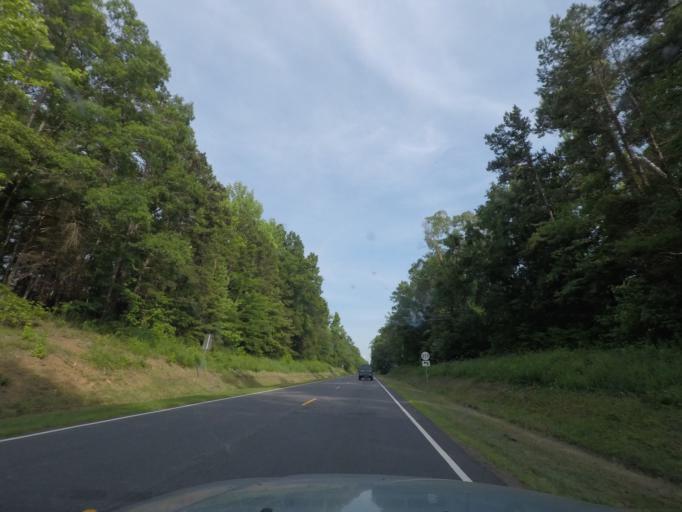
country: US
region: Virginia
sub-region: Mecklenburg County
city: Clarksville
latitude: 36.6934
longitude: -78.6226
